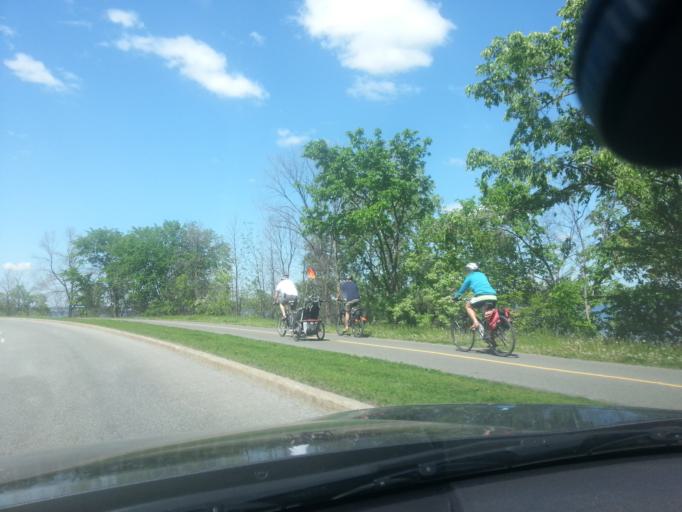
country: CA
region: Ontario
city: Ottawa
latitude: 45.3832
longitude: -75.7751
